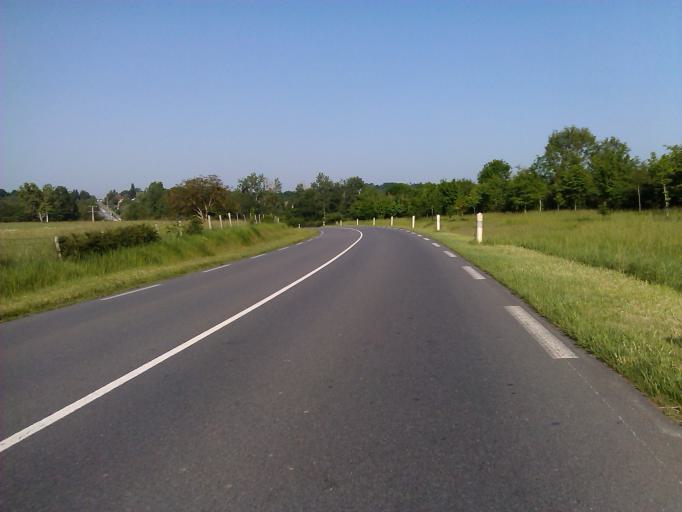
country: FR
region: Centre
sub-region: Departement de l'Indre
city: La Chatre
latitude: 46.5759
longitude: 1.9021
